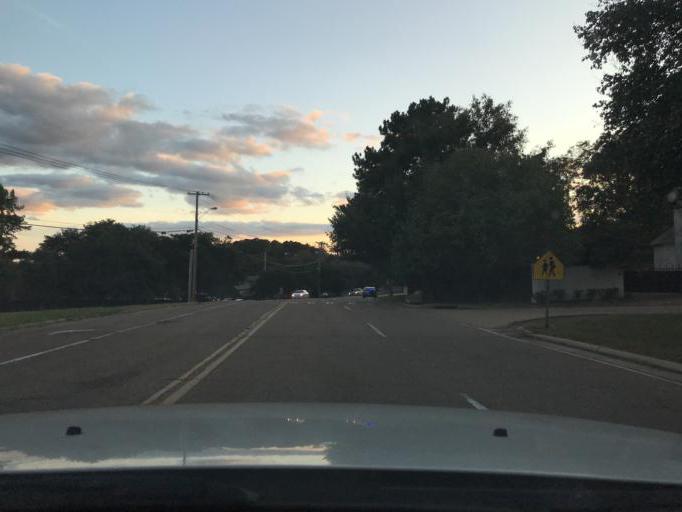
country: US
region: Mississippi
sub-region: Rankin County
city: Flowood
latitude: 32.3486
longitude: -90.1561
